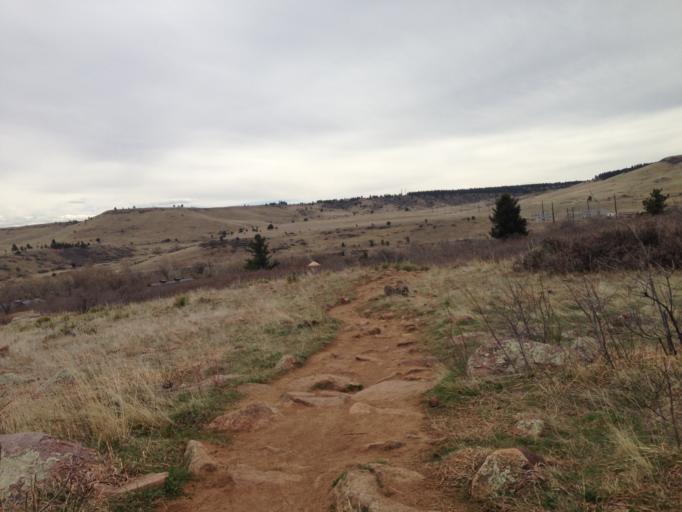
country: US
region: Colorado
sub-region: Boulder County
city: Boulder
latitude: 39.9427
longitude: -105.2623
